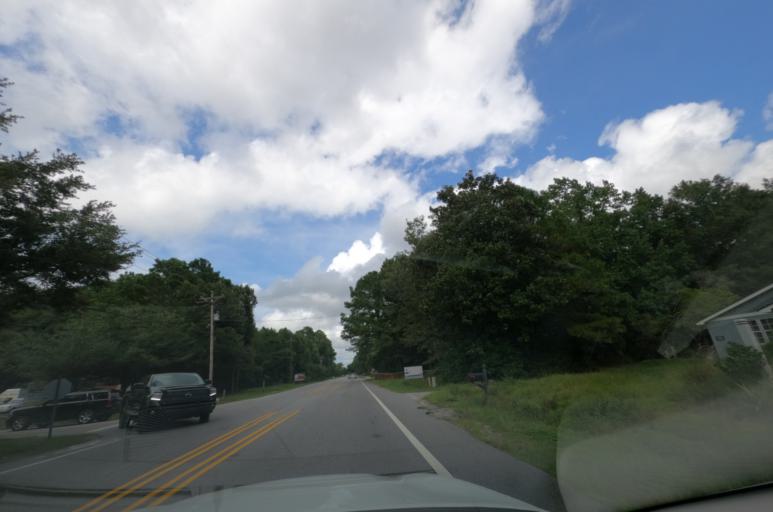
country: US
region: South Carolina
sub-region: Charleston County
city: Shell Point
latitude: 32.7294
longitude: -80.0652
